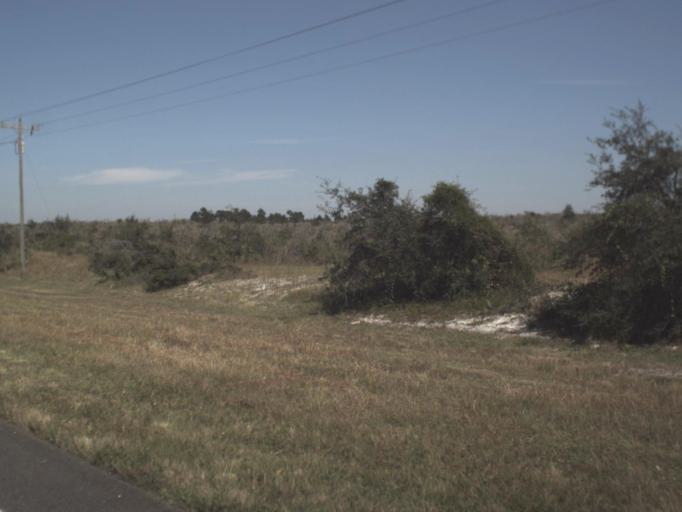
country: US
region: Florida
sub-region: Highlands County
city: Placid Lakes
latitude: 27.1146
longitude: -81.3313
